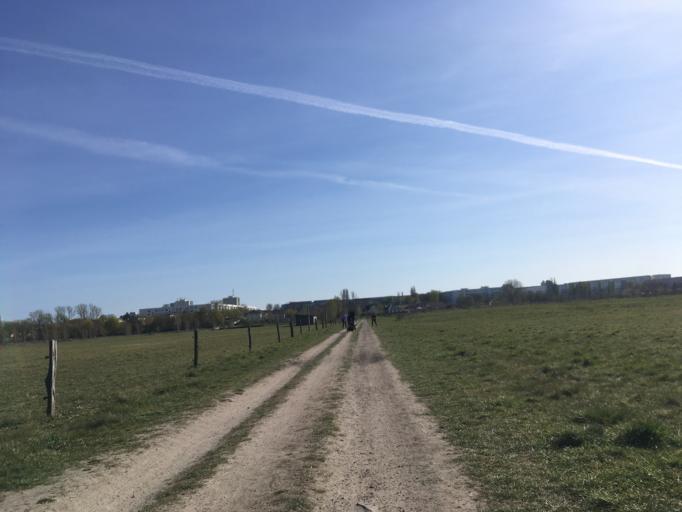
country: DE
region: Berlin
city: Wartenberg
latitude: 52.5826
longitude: 13.5092
